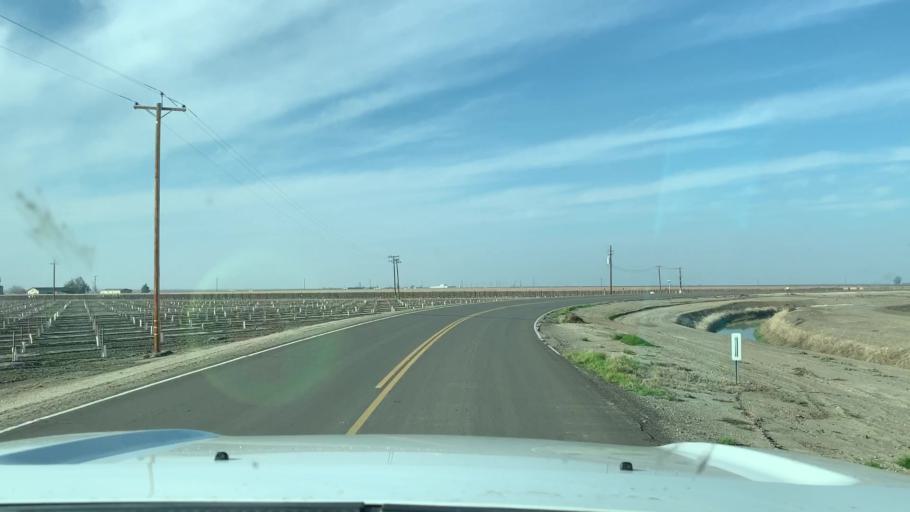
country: US
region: California
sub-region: Kern County
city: Buttonwillow
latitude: 35.4691
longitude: -119.5845
